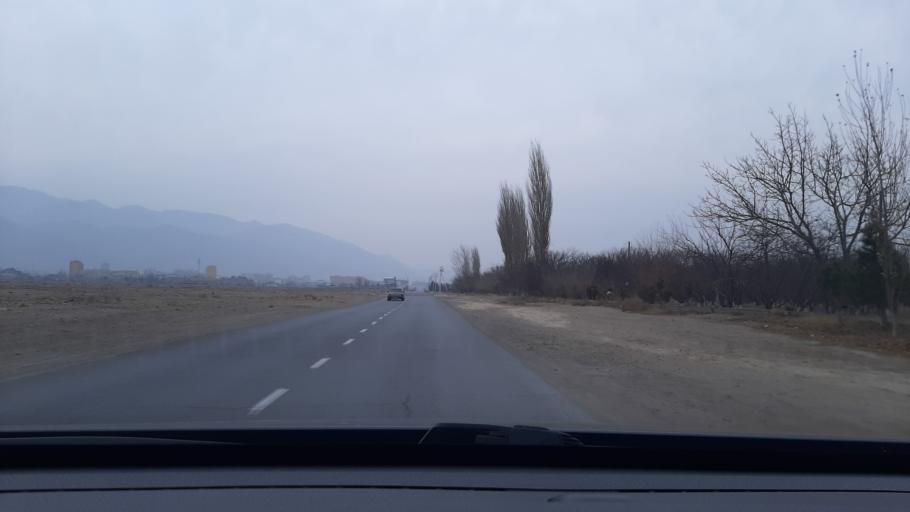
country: TJ
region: Viloyati Sughd
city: Khujand
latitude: 40.2723
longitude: 69.5760
